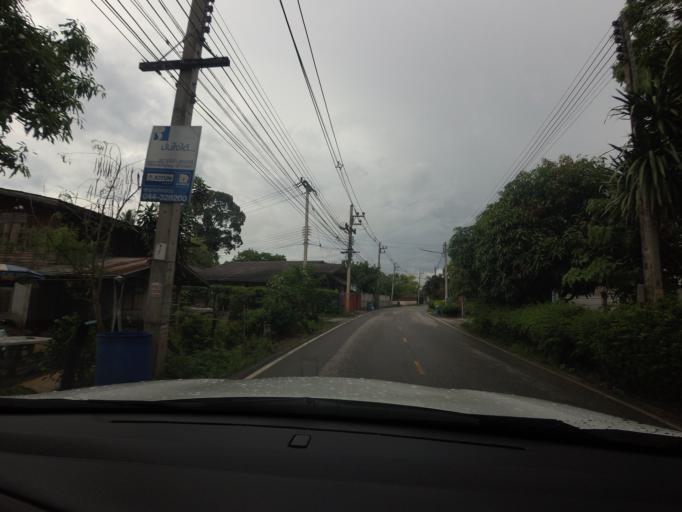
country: TH
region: Nakhon Ratchasima
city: Pak Chong
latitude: 14.6096
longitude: 101.4446
